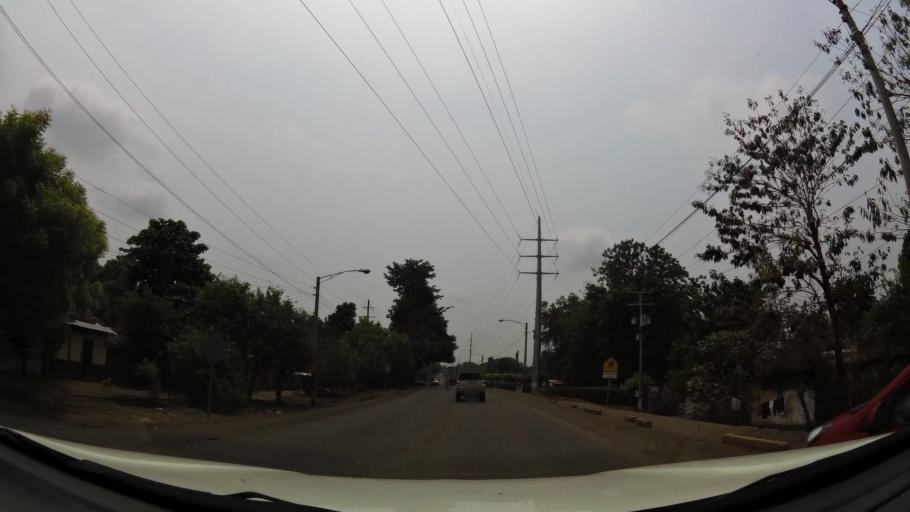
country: NI
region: Chinandega
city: Chinandega
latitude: 12.6367
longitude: -87.1210
